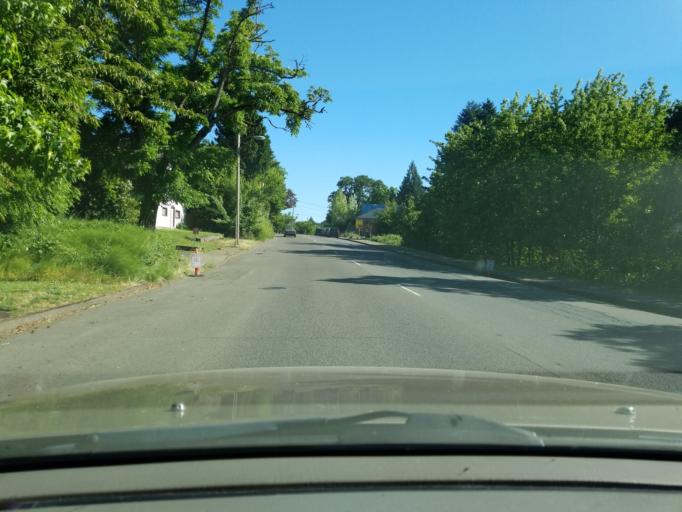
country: US
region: Oregon
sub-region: Yamhill County
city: McMinnville
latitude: 45.2077
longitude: -123.1991
